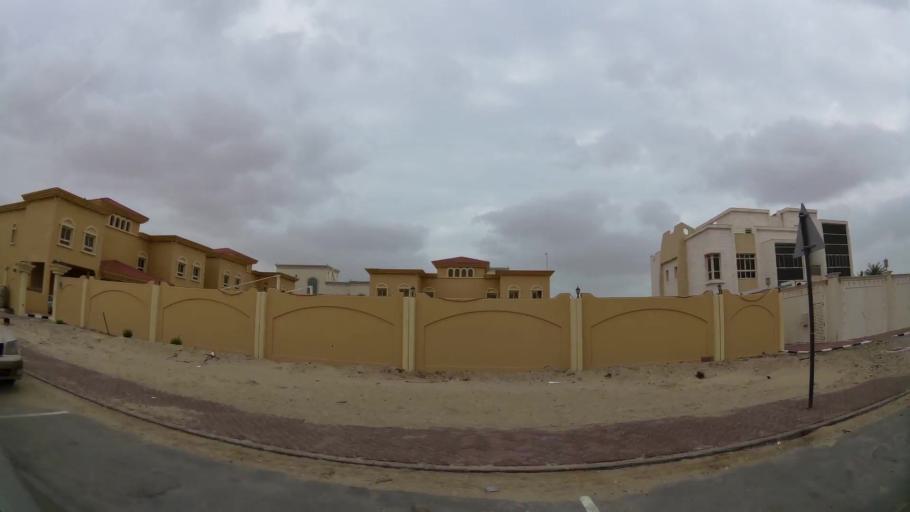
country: AE
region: Abu Dhabi
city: Abu Dhabi
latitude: 24.3787
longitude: 54.6491
